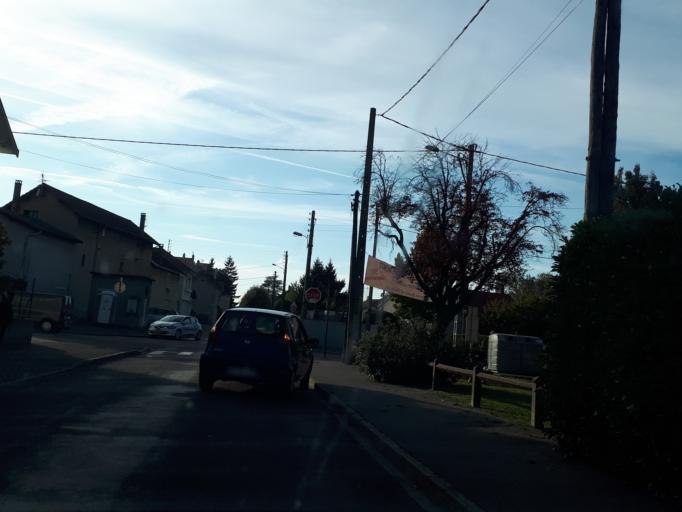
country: FR
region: Rhone-Alpes
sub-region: Departement de l'Isere
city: Bourgoin
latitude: 45.5917
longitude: 5.2857
